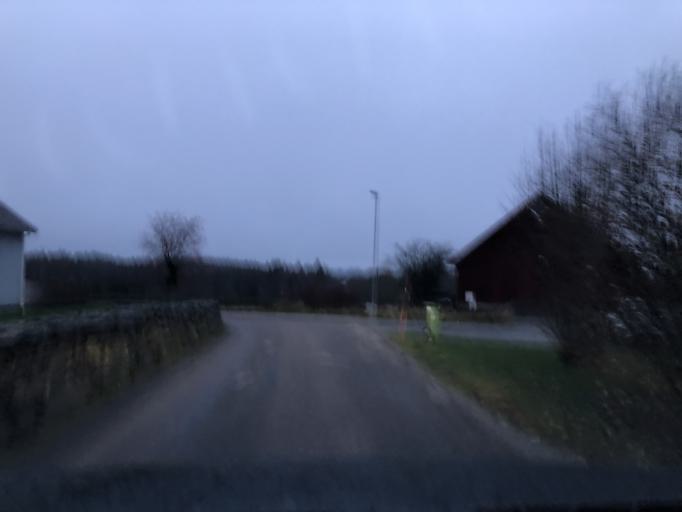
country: SE
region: Vaestra Goetaland
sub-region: Boras Kommun
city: Sjomarken
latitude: 57.7604
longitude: 12.8416
